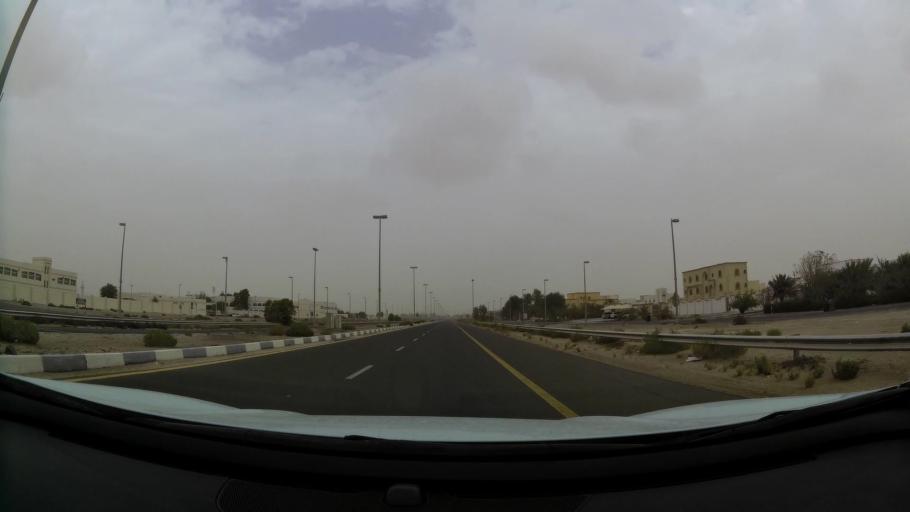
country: AE
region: Abu Dhabi
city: Abu Dhabi
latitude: 24.4046
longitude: 54.7342
